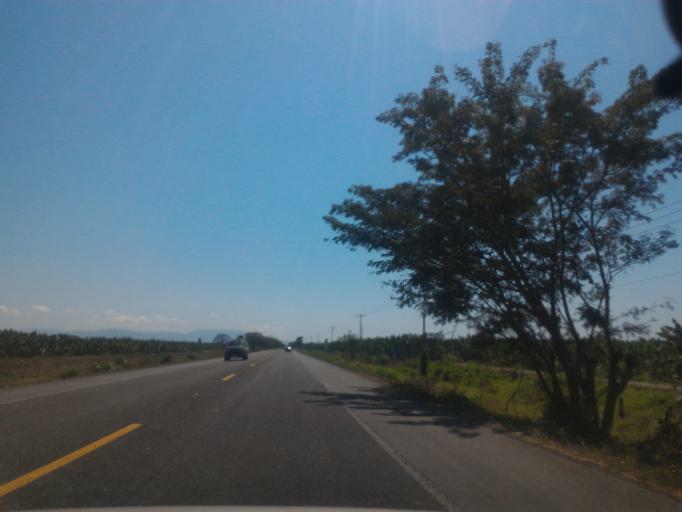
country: MX
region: Colima
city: Tecoman
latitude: 18.8138
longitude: -103.8053
